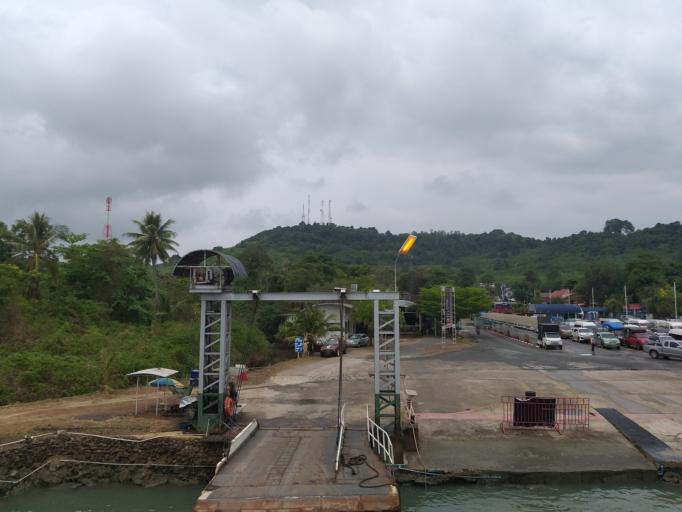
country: TH
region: Trat
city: Laem Ngop
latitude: 12.1869
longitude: 102.3011
